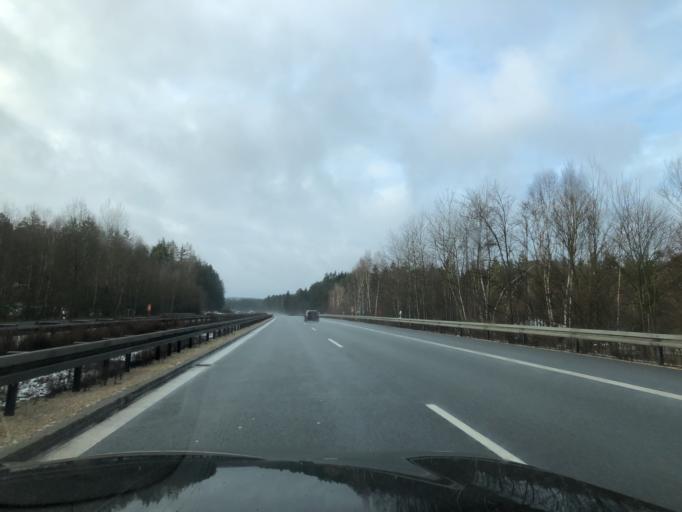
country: DE
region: Bavaria
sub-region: Upper Palatinate
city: Kummersbruck
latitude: 49.3963
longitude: 11.8619
